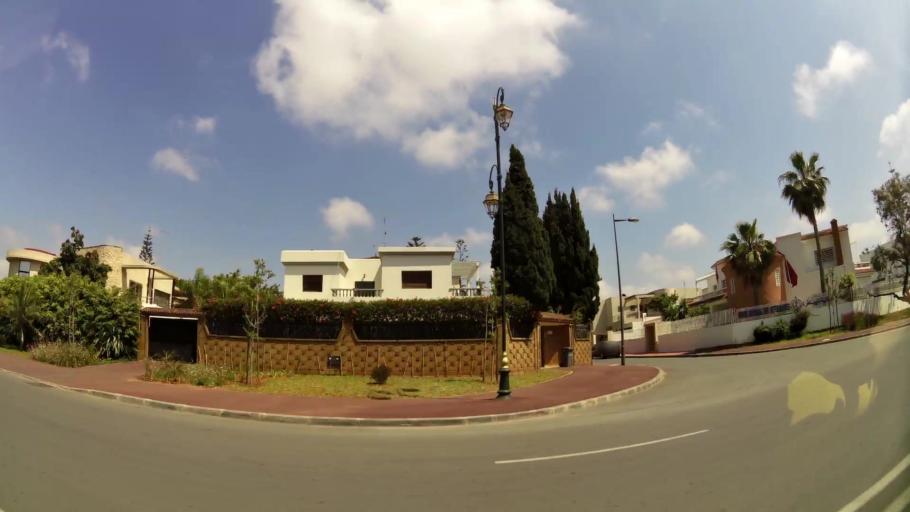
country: MA
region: Rabat-Sale-Zemmour-Zaer
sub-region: Skhirate-Temara
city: Temara
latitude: 33.9630
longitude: -6.8823
